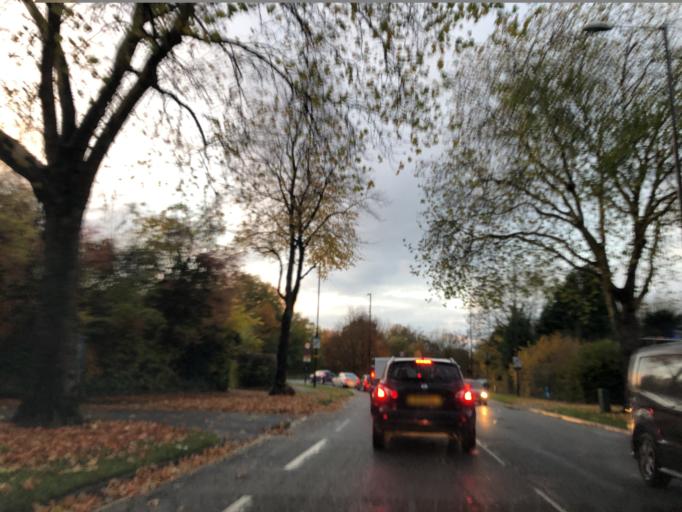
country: GB
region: England
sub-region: Coventry
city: Keresley
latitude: 52.4206
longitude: -1.5538
